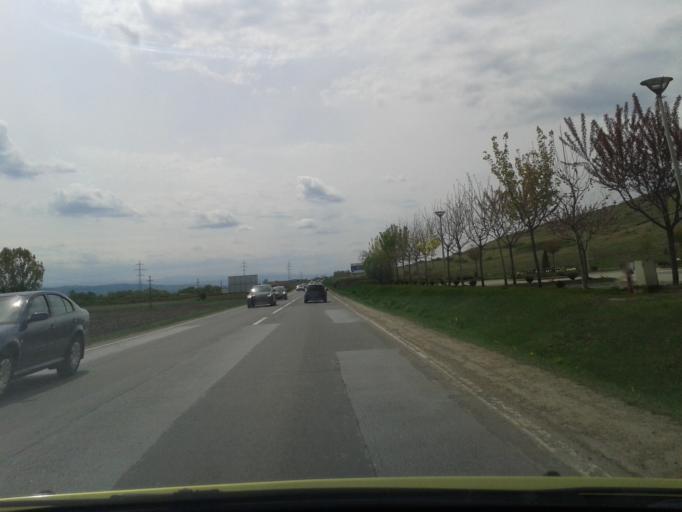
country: RO
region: Alba
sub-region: Comuna Santimbru
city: Santimbru
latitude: 46.1230
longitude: 23.6229
